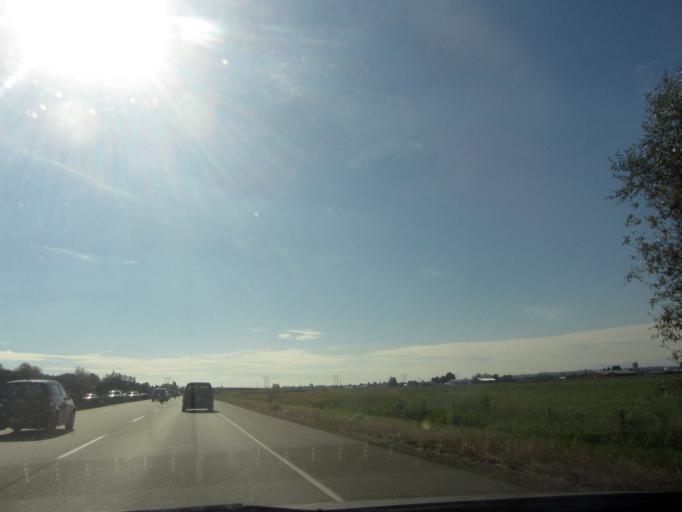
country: CA
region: British Columbia
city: Ladner
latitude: 49.1773
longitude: -123.0356
